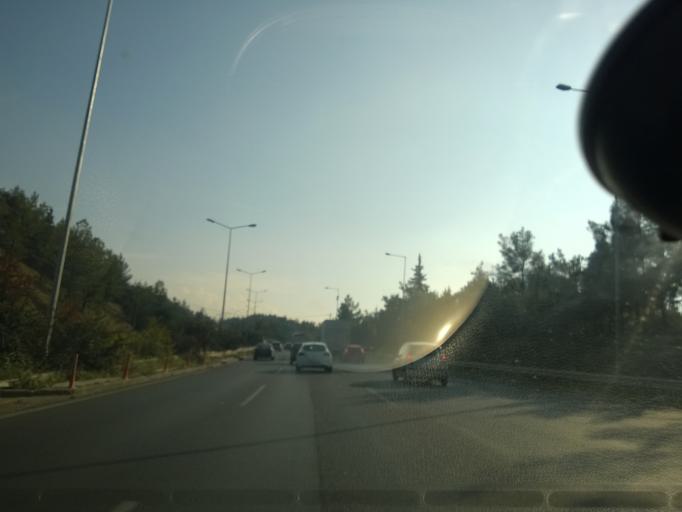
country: GR
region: Central Macedonia
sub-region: Nomos Thessalonikis
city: Agios Pavlos
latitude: 40.6519
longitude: 22.9663
